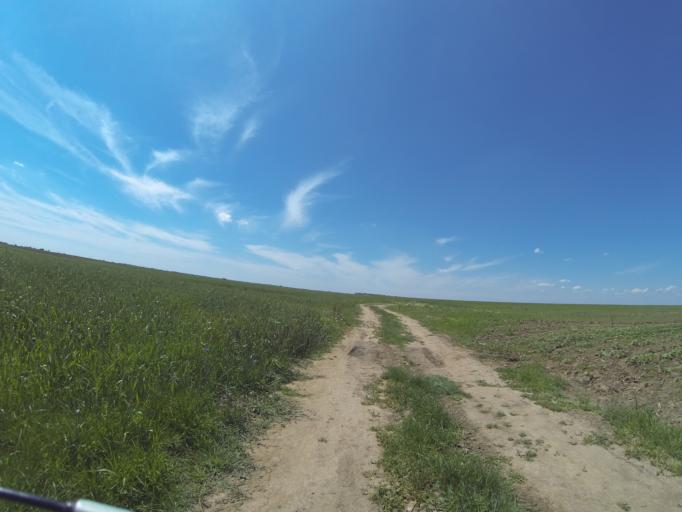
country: RO
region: Dolj
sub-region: Comuna Leu
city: Leu
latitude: 44.2176
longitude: 24.0158
